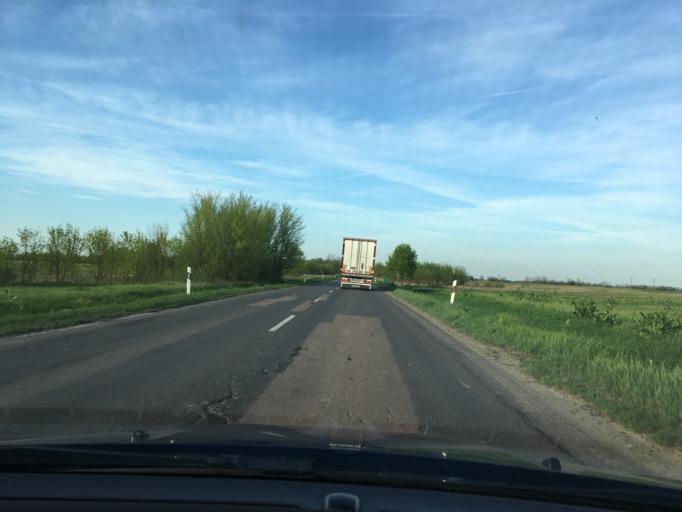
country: HU
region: Hajdu-Bihar
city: Berettyoujfalu
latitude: 47.1698
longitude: 21.5159
